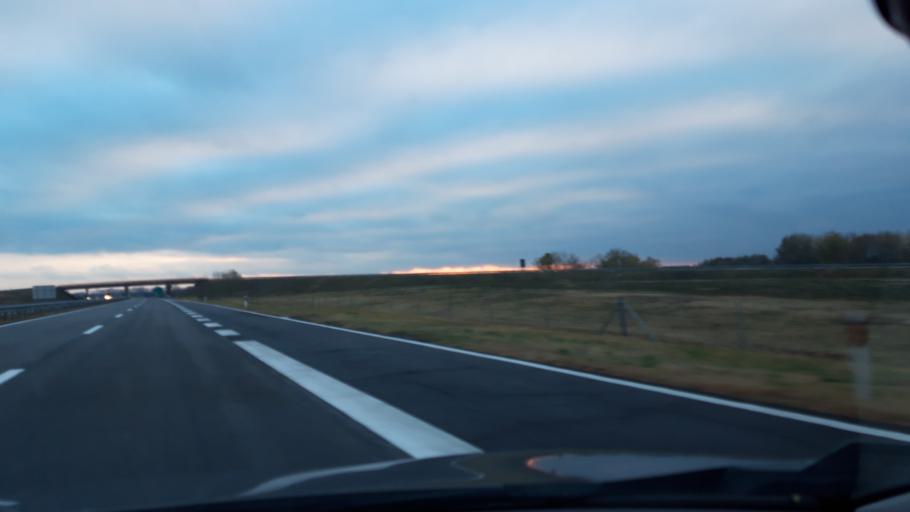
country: RS
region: Autonomna Pokrajina Vojvodina
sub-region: Severnobacki Okrug
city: Mali Igos
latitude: 45.6461
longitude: 19.7167
